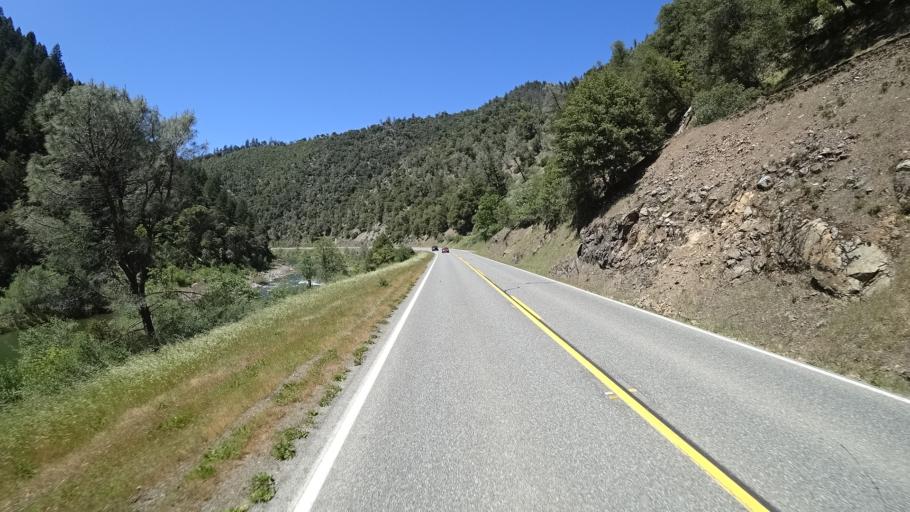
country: US
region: California
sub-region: Trinity County
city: Hayfork
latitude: 40.7652
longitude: -123.2916
